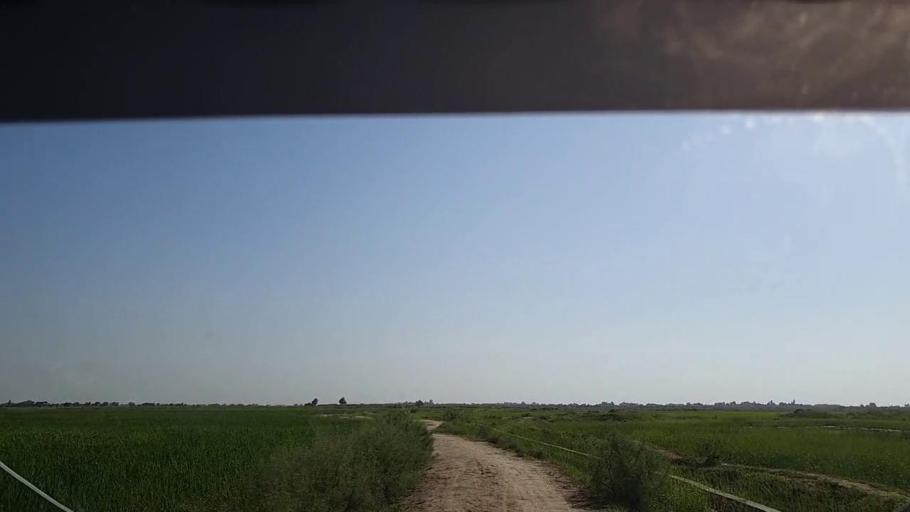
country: PK
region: Sindh
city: Ghauspur
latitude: 28.1771
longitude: 69.0371
